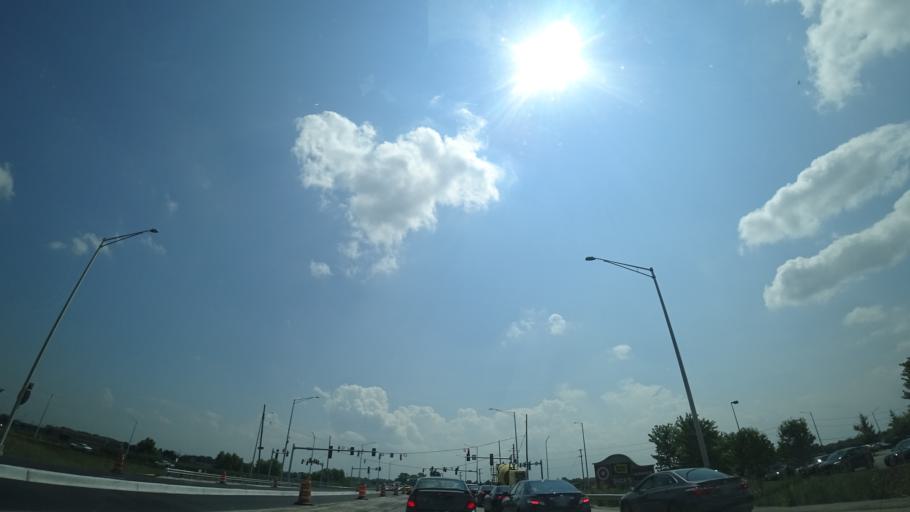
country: US
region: Illinois
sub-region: Will County
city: Frankfort Square
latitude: 41.5446
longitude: -87.7924
